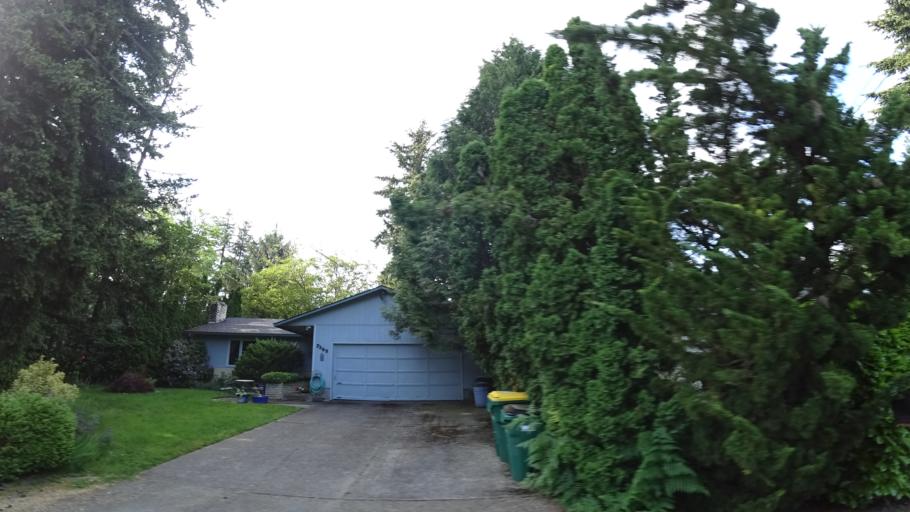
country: US
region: Oregon
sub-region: Washington County
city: Garden Home-Whitford
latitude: 45.4604
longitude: -122.7519
